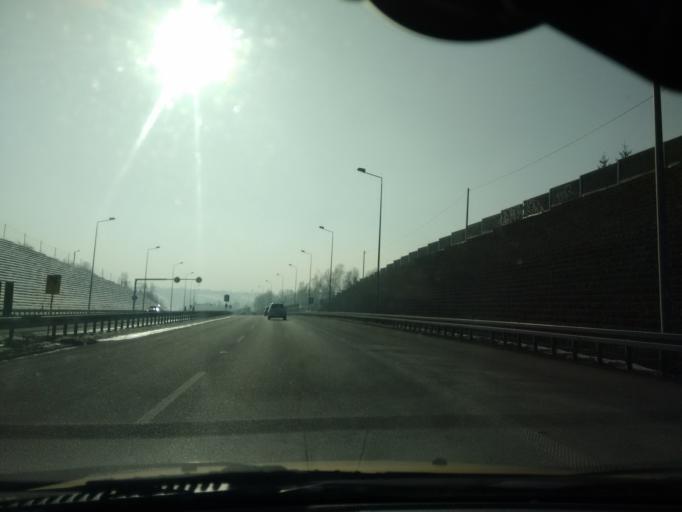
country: PL
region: Silesian Voivodeship
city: Janowice
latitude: 49.8411
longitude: 19.0894
